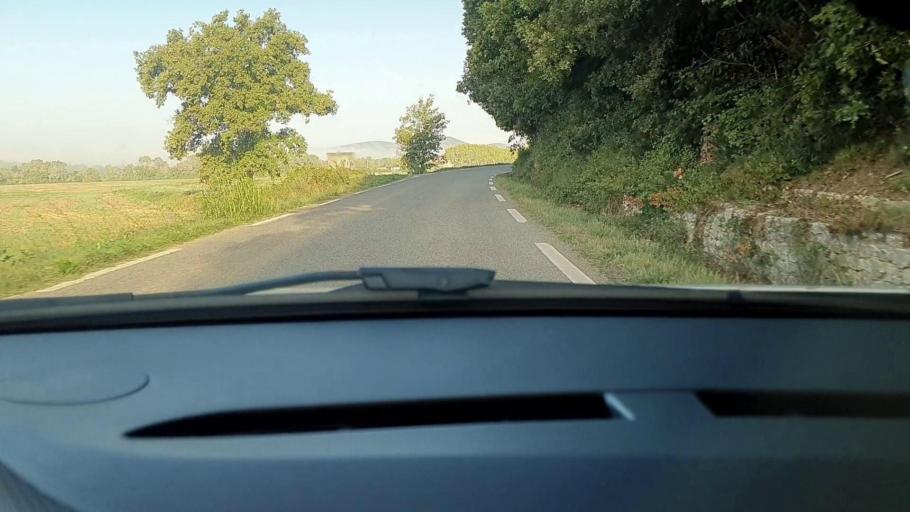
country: FR
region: Languedoc-Roussillon
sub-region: Departement du Gard
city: Barjac
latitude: 44.2461
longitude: 4.2950
